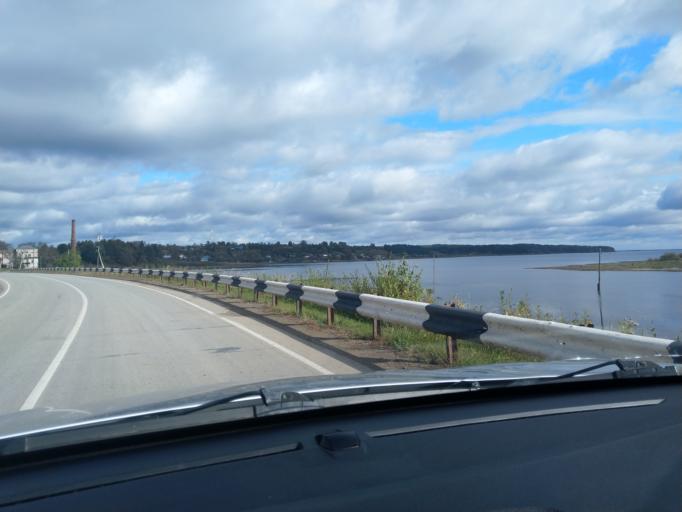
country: RU
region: Perm
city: Pozhva
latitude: 59.0796
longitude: 56.0804
